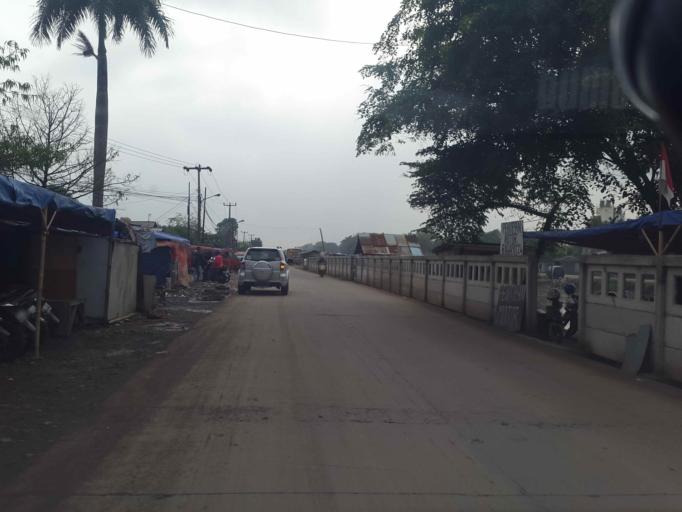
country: ID
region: West Java
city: Cikarang
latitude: -6.2807
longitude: 107.0871
